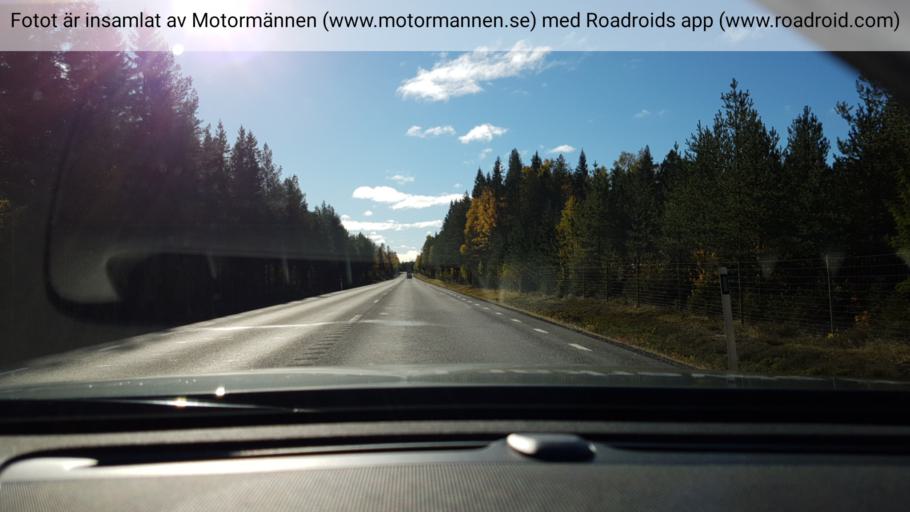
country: SE
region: Vaesterbotten
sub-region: Skelleftea Kommun
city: Burea
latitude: 64.5780
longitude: 21.2221
